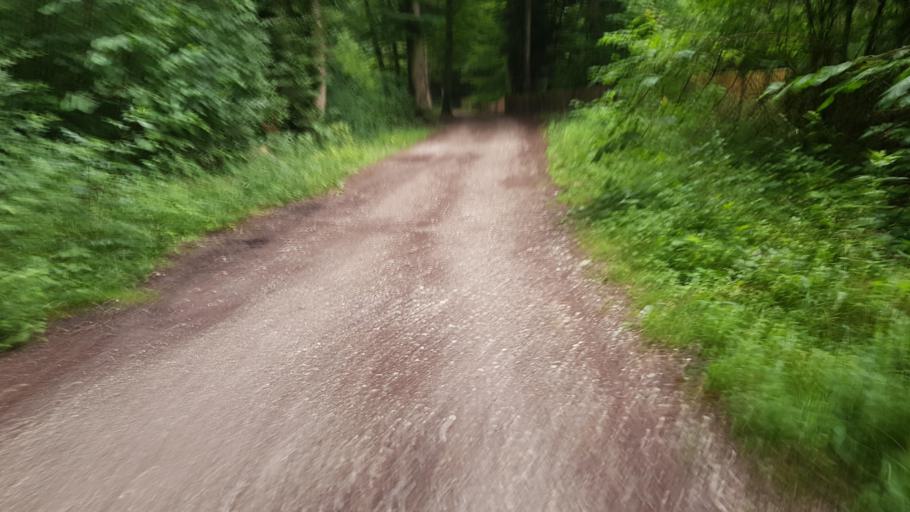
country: DE
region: Bavaria
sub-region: Upper Bavaria
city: Gauting
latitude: 48.0457
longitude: 11.3701
